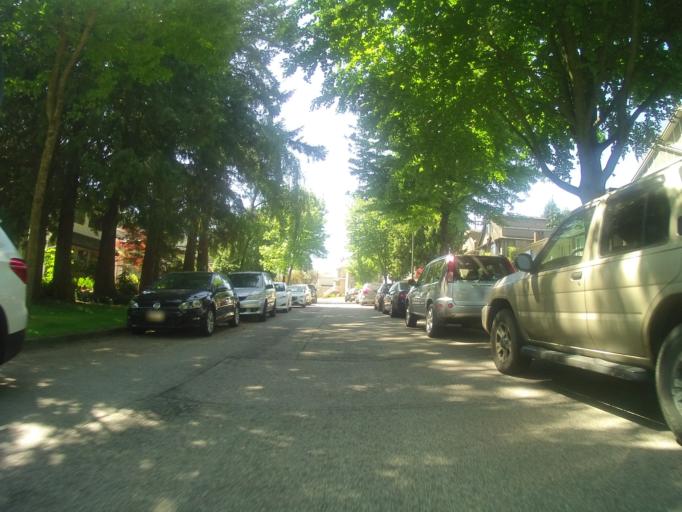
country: CA
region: British Columbia
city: Vancouver
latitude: 49.2134
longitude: -123.1115
